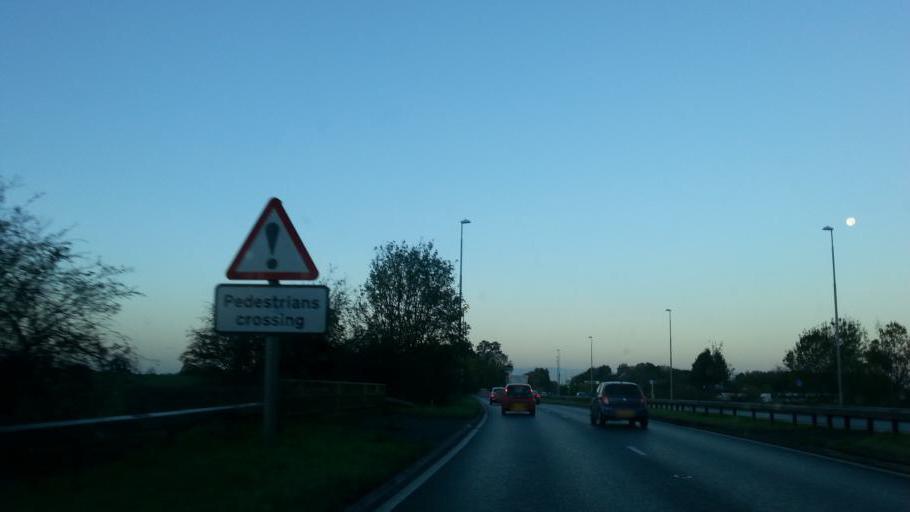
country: GB
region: England
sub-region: Nottinghamshire
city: Radcliffe on Trent
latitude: 52.9360
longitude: -1.0742
